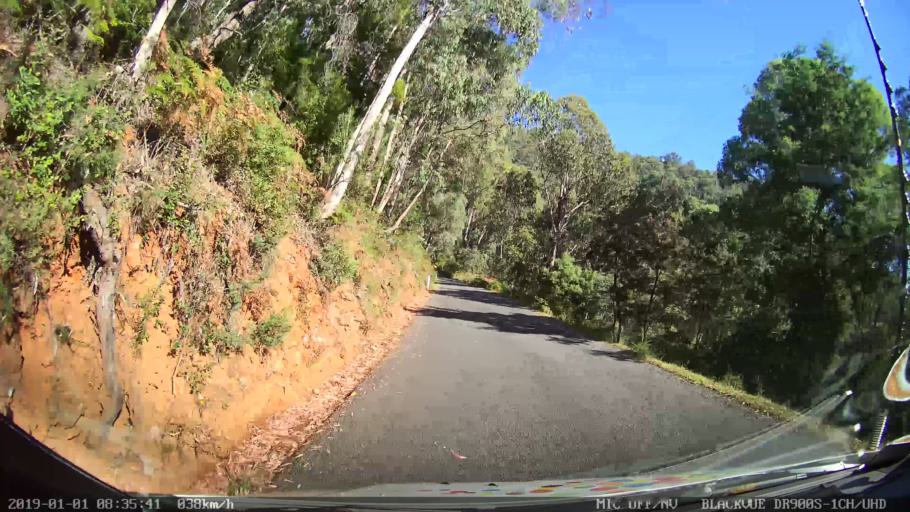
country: AU
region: New South Wales
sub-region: Snowy River
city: Jindabyne
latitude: -36.3479
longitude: 148.1939
